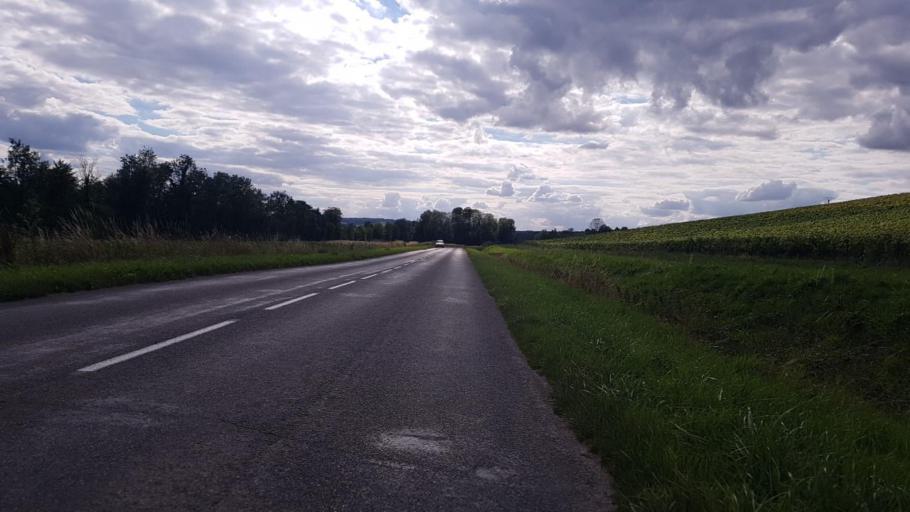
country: FR
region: Picardie
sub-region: Departement de l'Aisne
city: Brasles
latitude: 49.0462
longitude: 3.4437
